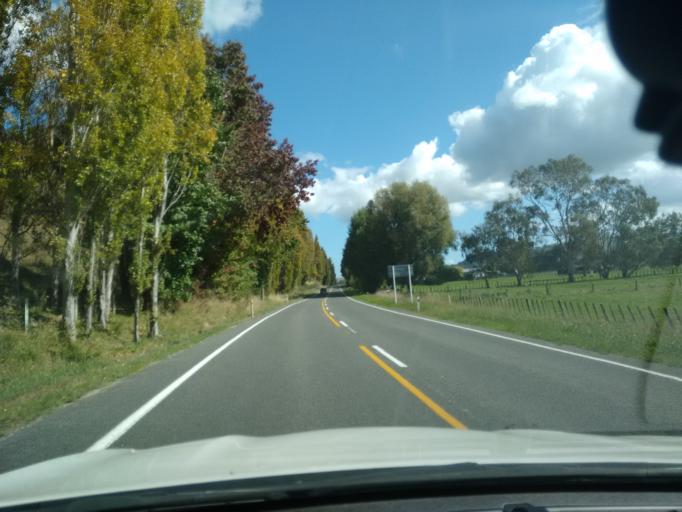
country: NZ
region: Manawatu-Wanganui
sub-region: Wanganui District
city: Wanganui
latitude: -39.8963
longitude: 175.1020
